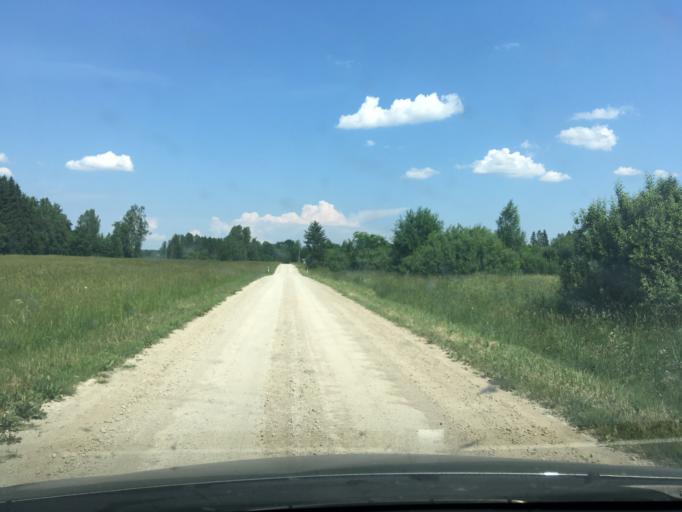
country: EE
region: Raplamaa
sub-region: Maerjamaa vald
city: Marjamaa
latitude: 58.8069
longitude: 24.4332
